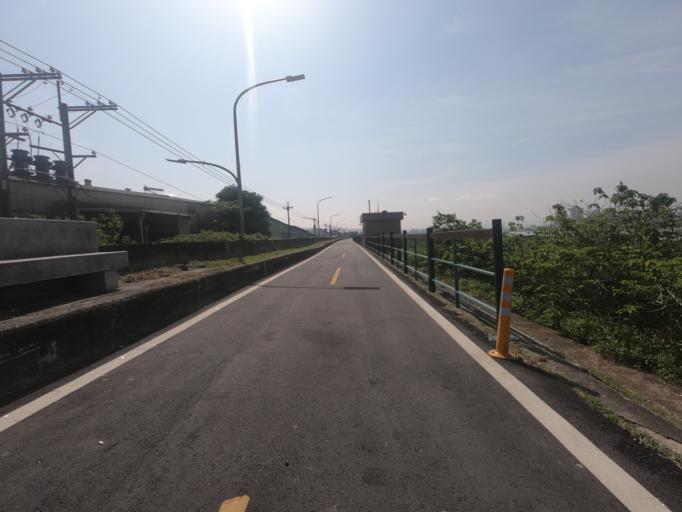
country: TW
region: Taipei
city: Taipei
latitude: 25.1040
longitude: 121.4802
